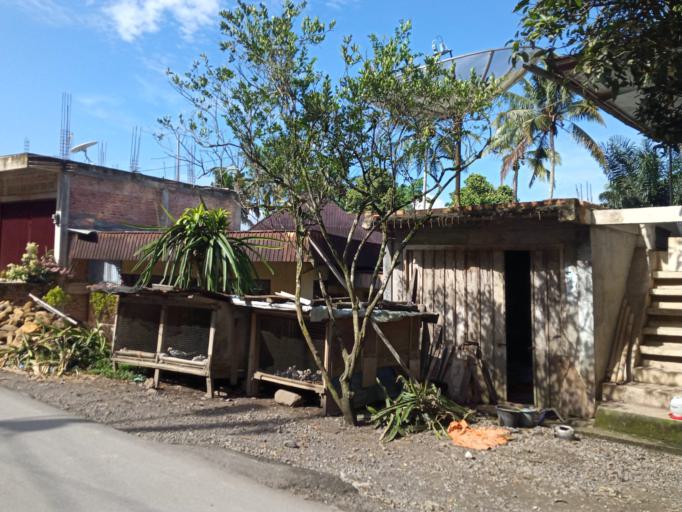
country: ID
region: Jambi
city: Sungai Penuh
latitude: -2.1649
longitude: 101.5922
